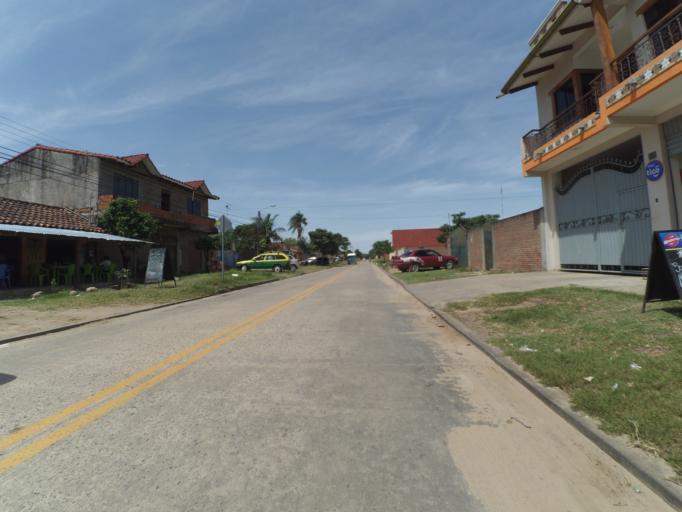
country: BO
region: Santa Cruz
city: Santa Cruz de la Sierra
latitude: -17.8226
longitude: -63.2251
